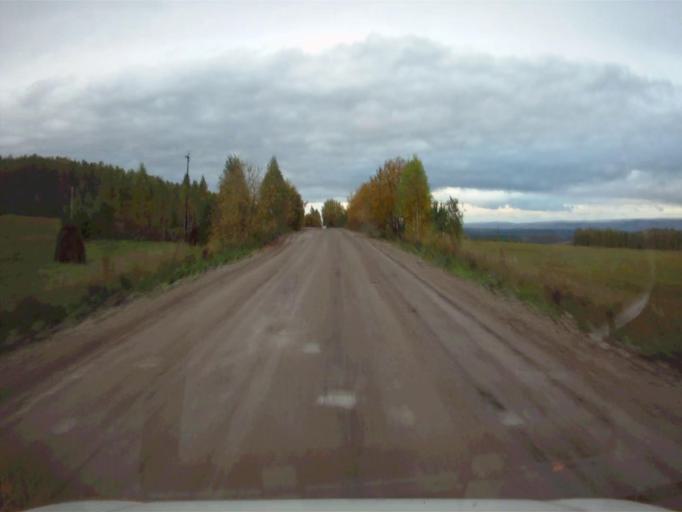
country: RU
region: Sverdlovsk
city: Mikhaylovsk
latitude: 56.2003
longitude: 59.2003
